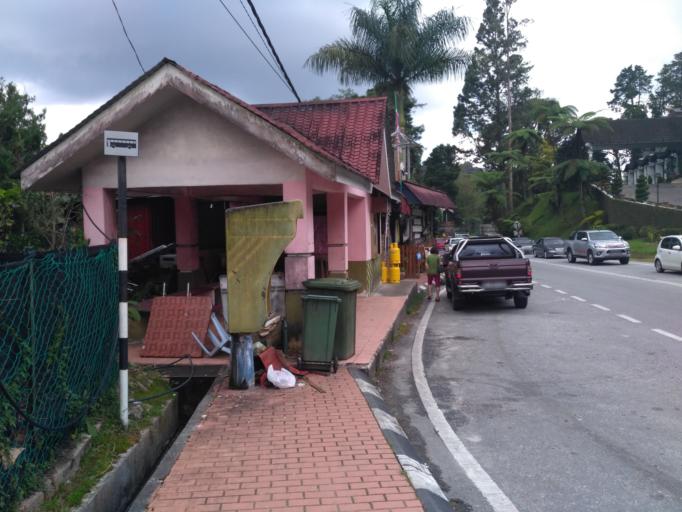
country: MY
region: Pahang
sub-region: Cameron Highlands
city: Tanah Rata
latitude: 4.4854
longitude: 101.3778
